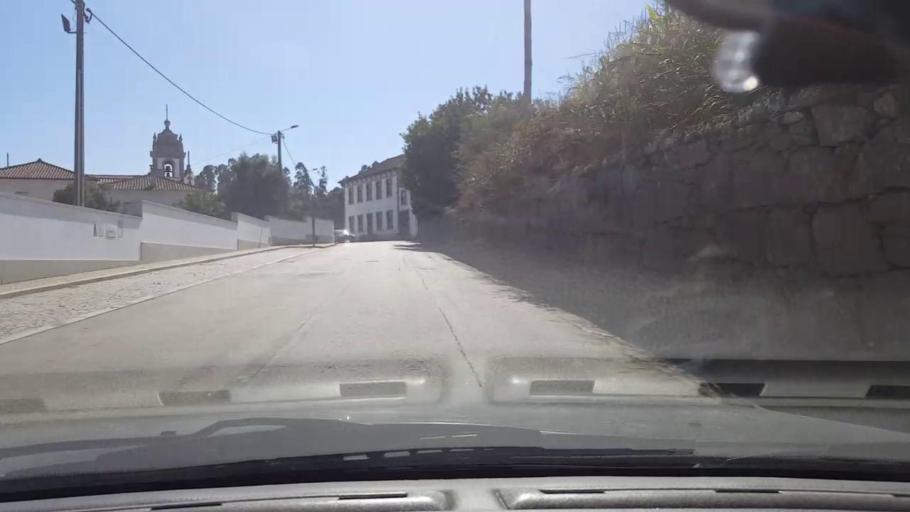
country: PT
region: Porto
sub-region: Matosinhos
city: Lavra
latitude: 41.2638
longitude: -8.6903
